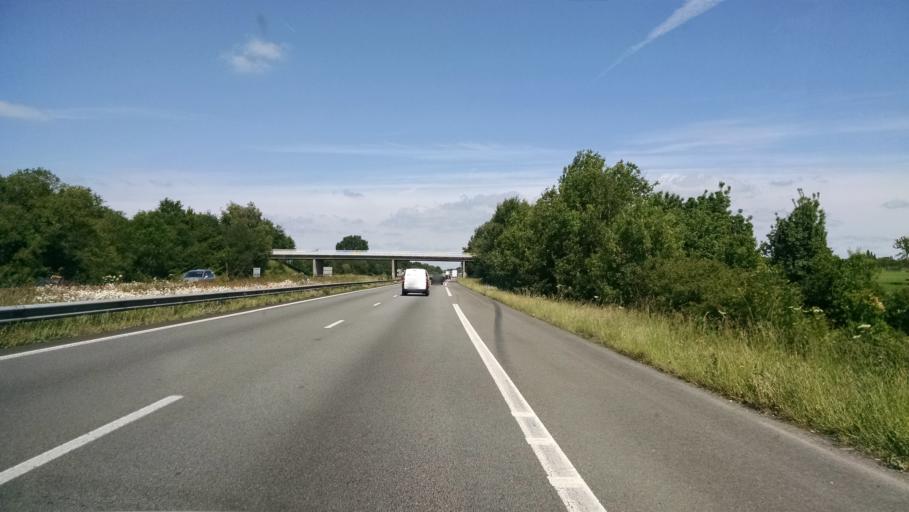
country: FR
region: Pays de la Loire
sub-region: Departement de la Loire-Atlantique
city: Sautron
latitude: 47.2683
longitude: -1.7123
